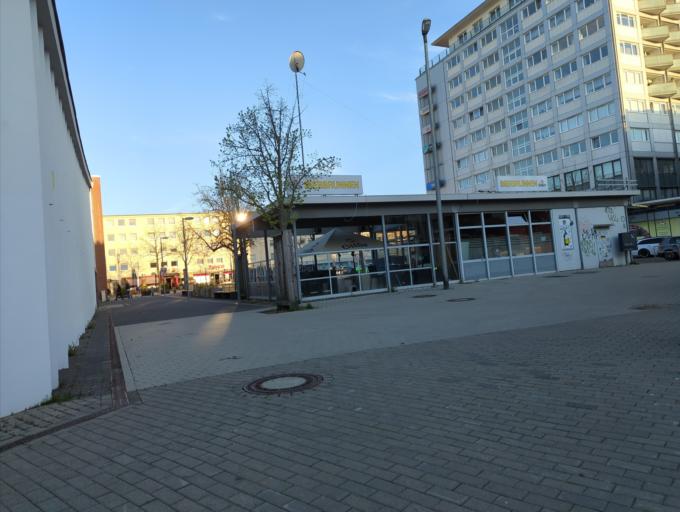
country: DE
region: Lower Saxony
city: Wolfsburg
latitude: 52.4268
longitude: 10.7891
